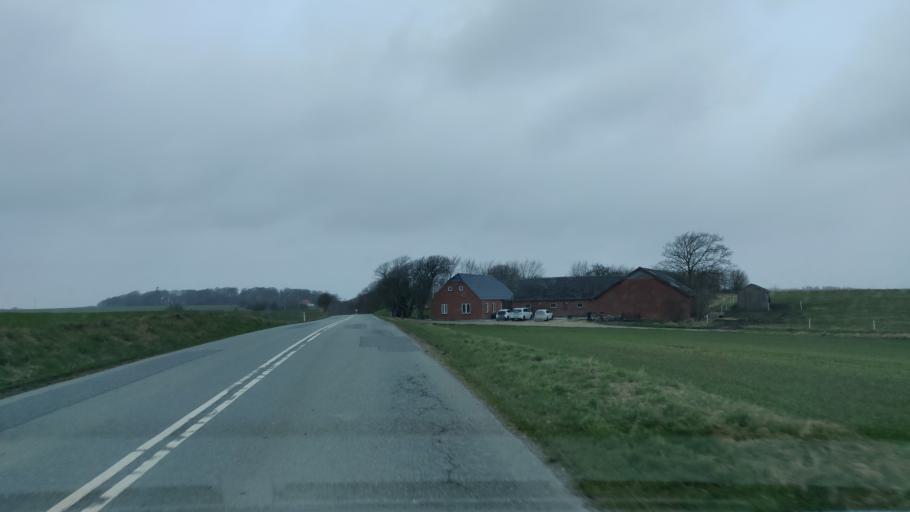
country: DK
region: Central Jutland
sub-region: Skive Kommune
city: Hojslev
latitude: 56.5876
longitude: 9.2236
